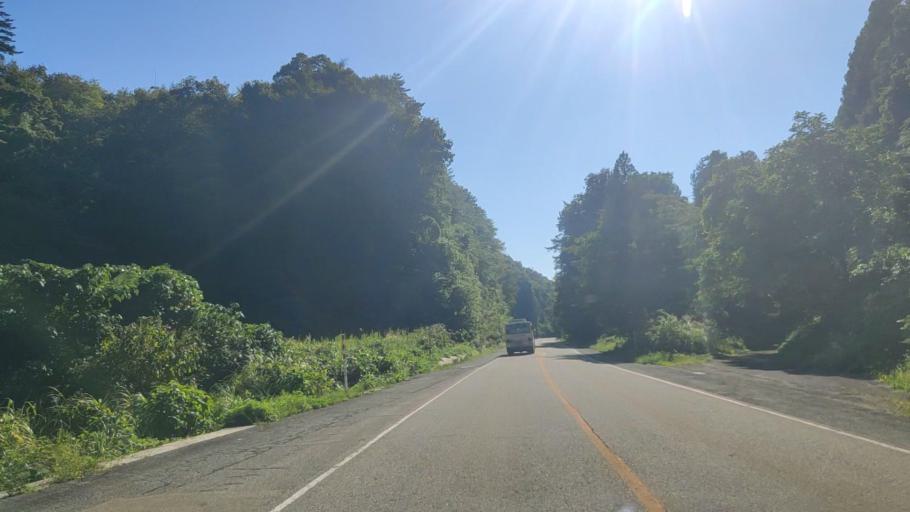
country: JP
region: Ishikawa
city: Nanao
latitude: 37.2465
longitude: 136.9930
